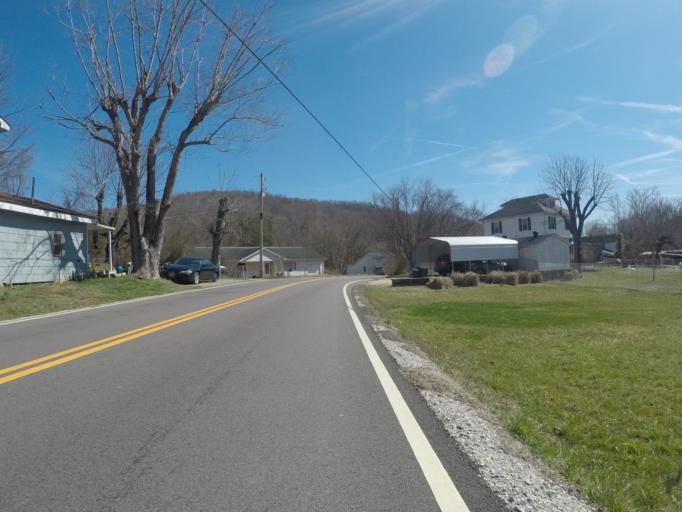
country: US
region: Ohio
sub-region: Lawrence County
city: Burlington
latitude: 38.4471
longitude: -82.5053
